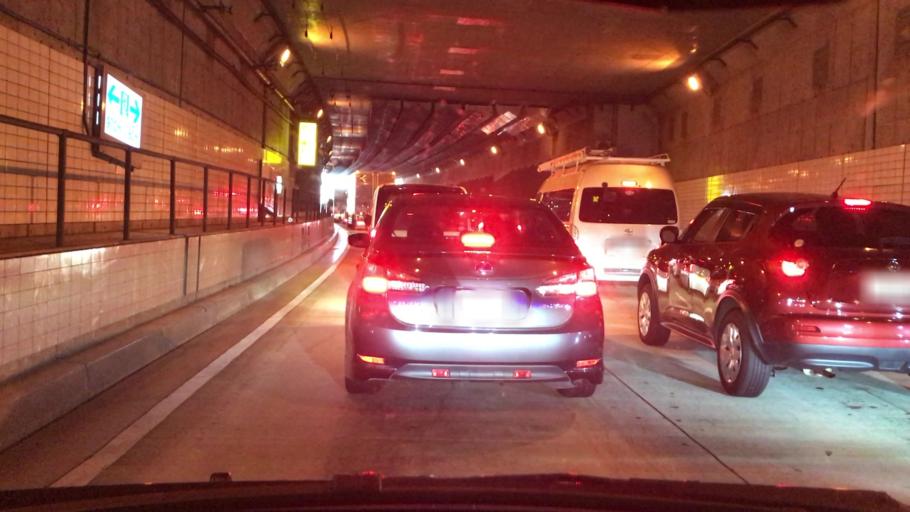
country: JP
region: Hyogo
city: Kobe
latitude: 34.7019
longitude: 135.2024
